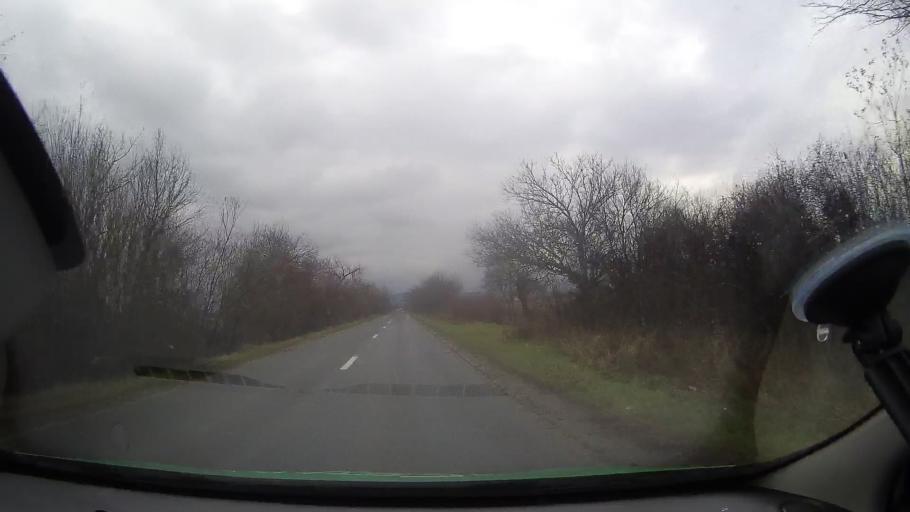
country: RO
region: Arad
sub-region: Comuna Sebis
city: Sebis
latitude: 46.3566
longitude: 22.1305
